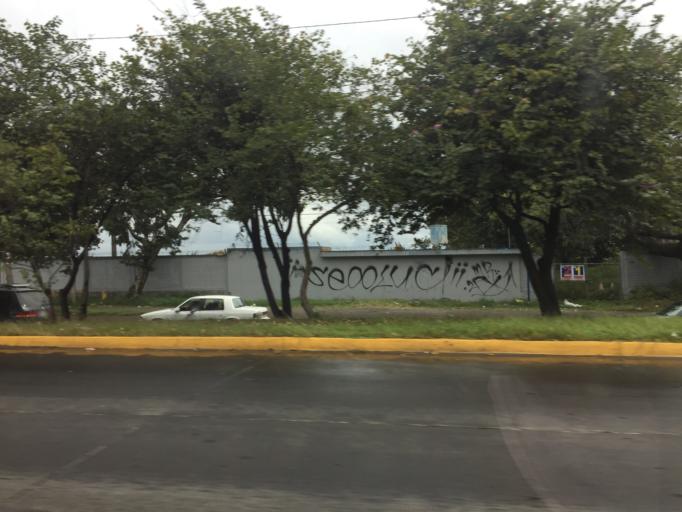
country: MX
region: Jalisco
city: Tlaquepaque
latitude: 20.6244
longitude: -103.3076
